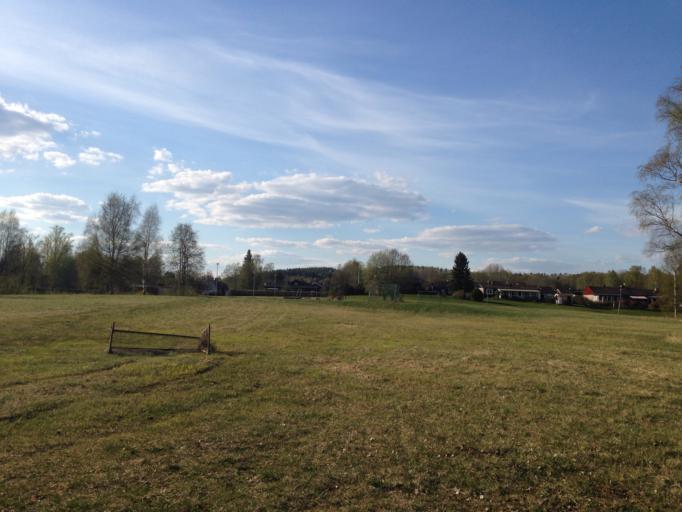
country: SE
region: Dalarna
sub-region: Ludvika Kommun
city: Ludvika
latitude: 60.1805
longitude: 15.1586
